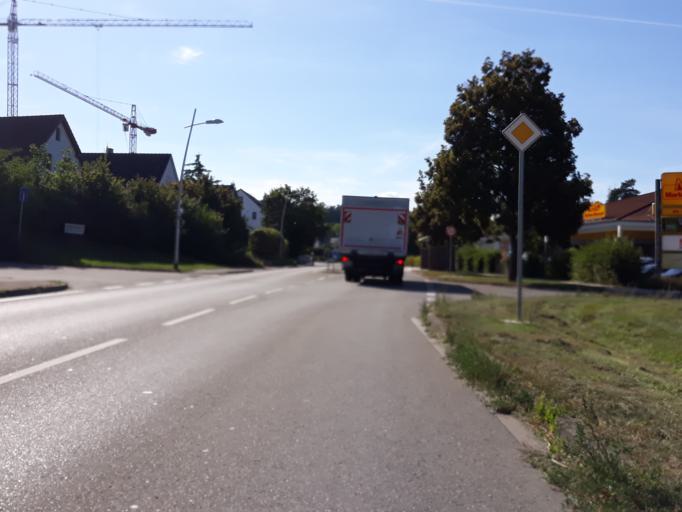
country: DE
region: Baden-Wuerttemberg
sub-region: Regierungsbezirk Stuttgart
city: Aidlingen
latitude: 48.7165
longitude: 8.8942
